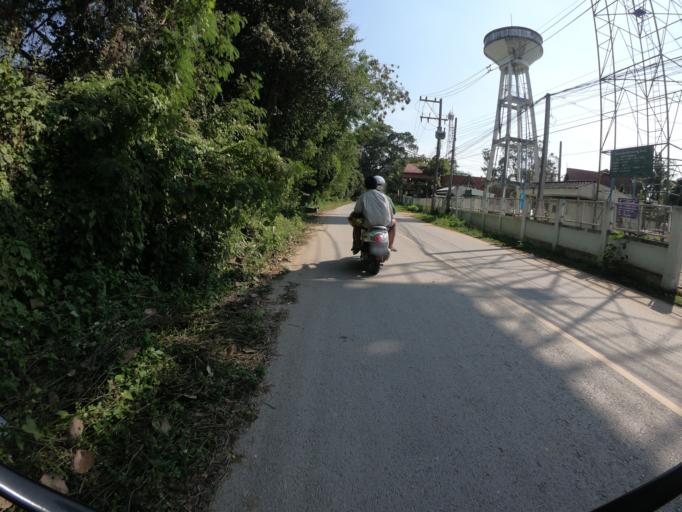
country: TH
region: Chiang Mai
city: San Sai
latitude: 18.8441
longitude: 99.0050
